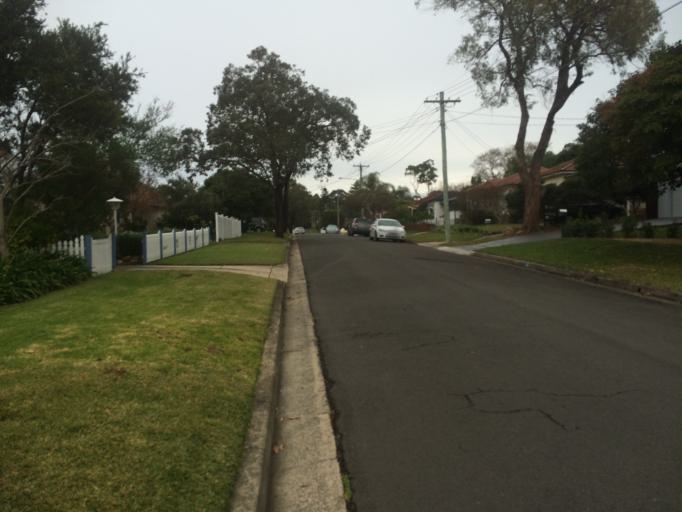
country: AU
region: New South Wales
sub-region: Sutherland Shire
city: Kirrawee
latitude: -34.0283
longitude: 151.0687
